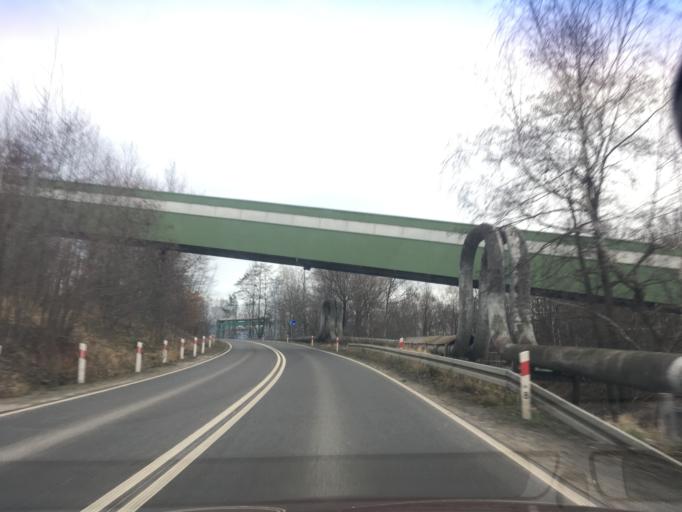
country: PL
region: Lower Silesian Voivodeship
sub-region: Powiat zgorzelecki
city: Bogatynia
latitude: 50.9293
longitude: 14.9272
